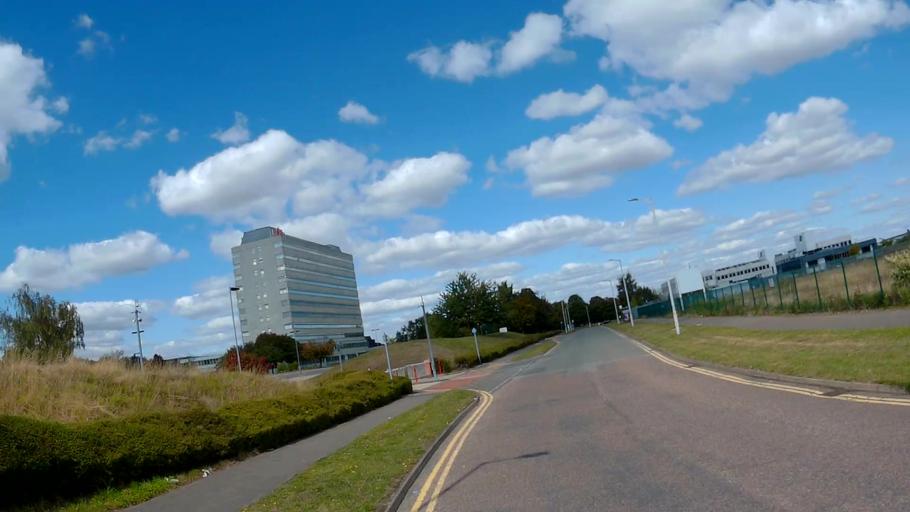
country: GB
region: England
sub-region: Bracknell Forest
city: Bracknell
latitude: 51.4065
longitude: -0.7743
